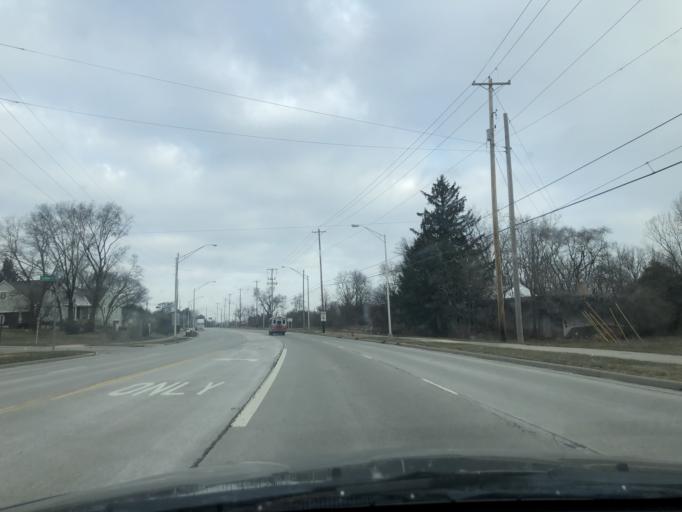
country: US
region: Ohio
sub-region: Franklin County
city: Obetz
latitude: 39.9123
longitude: -82.9285
